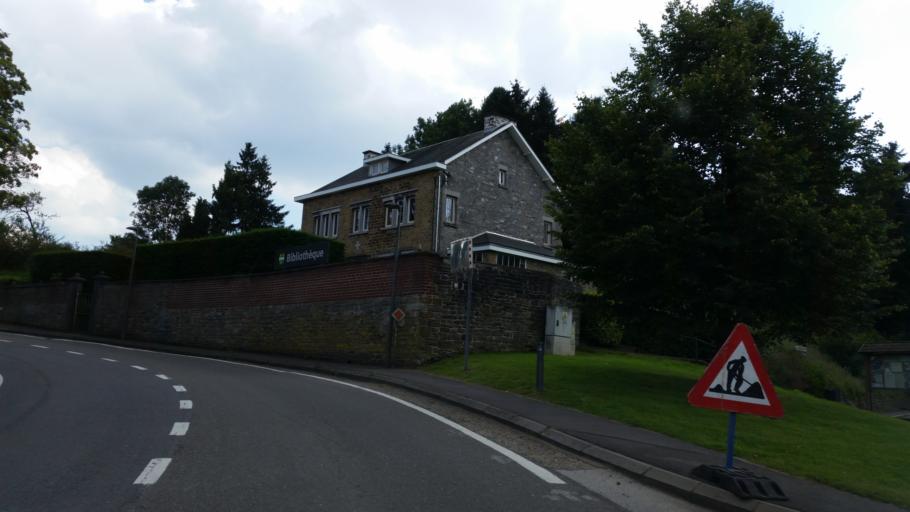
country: BE
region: Wallonia
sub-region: Province de Liege
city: Anthisnes
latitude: 50.4874
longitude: 5.5012
